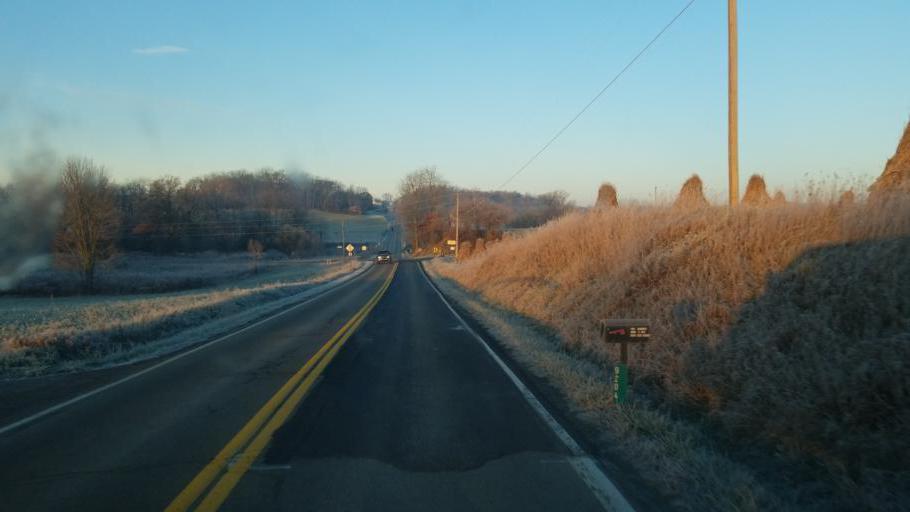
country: US
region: Ohio
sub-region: Wayne County
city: Apple Creek
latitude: 40.6895
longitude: -81.8637
